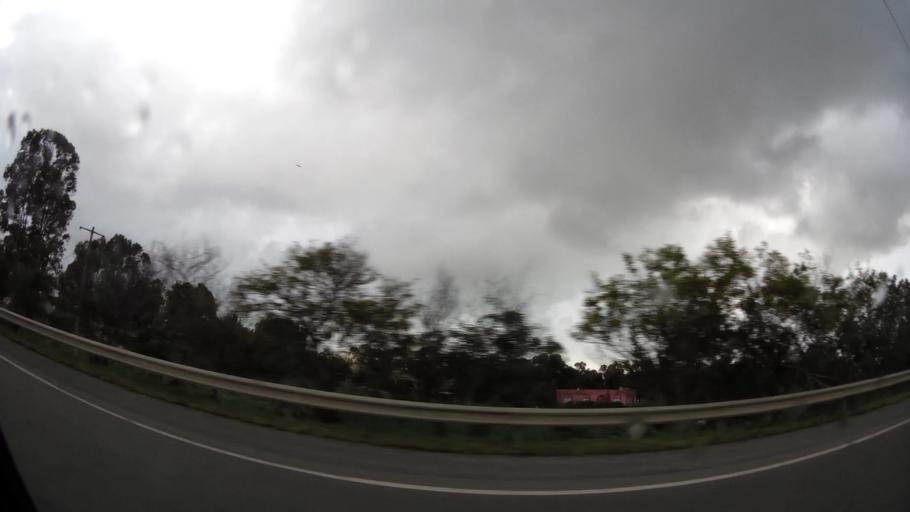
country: MA
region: Grand Casablanca
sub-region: Mohammedia
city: Mohammedia
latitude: 33.6462
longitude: -7.4210
